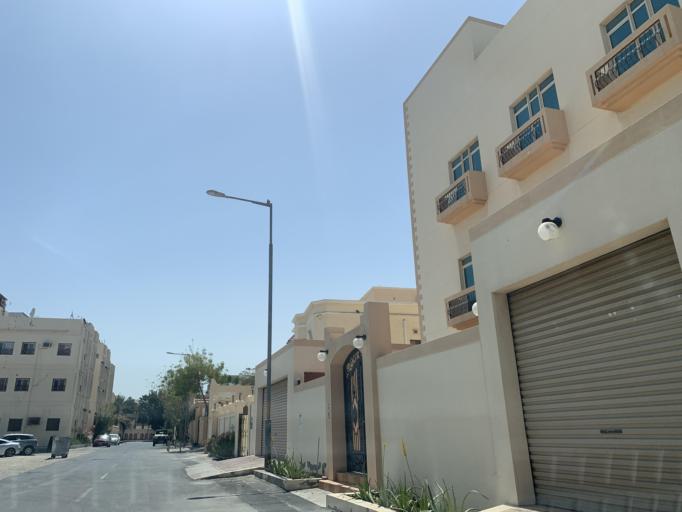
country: BH
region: Manama
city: Manama
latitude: 26.2112
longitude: 50.5807
